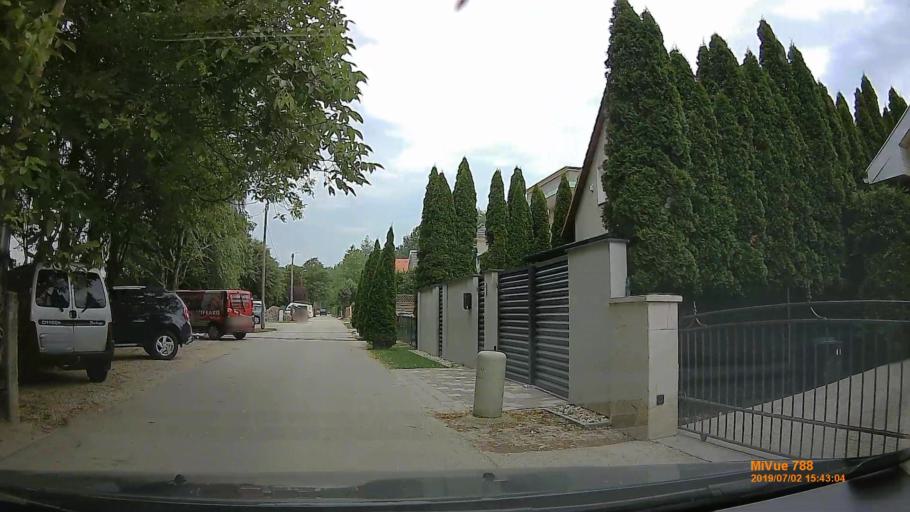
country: HU
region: Gyor-Moson-Sopron
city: Mosonmagyarovar
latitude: 47.8717
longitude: 17.2907
